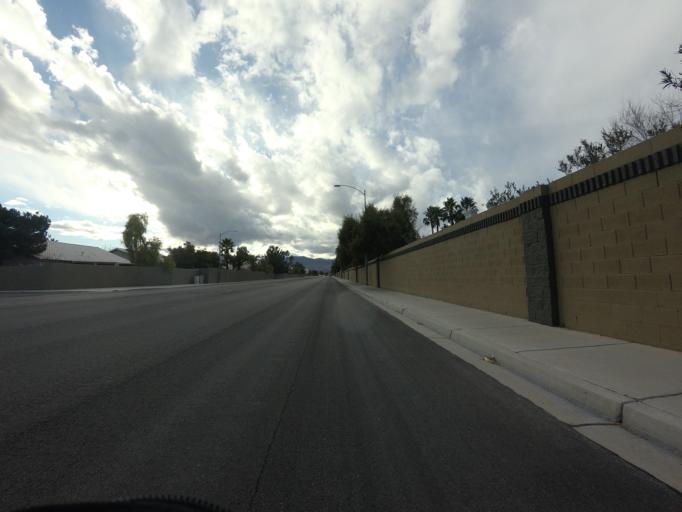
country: US
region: Nevada
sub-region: Clark County
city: Las Vegas
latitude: 36.2698
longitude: -115.2437
